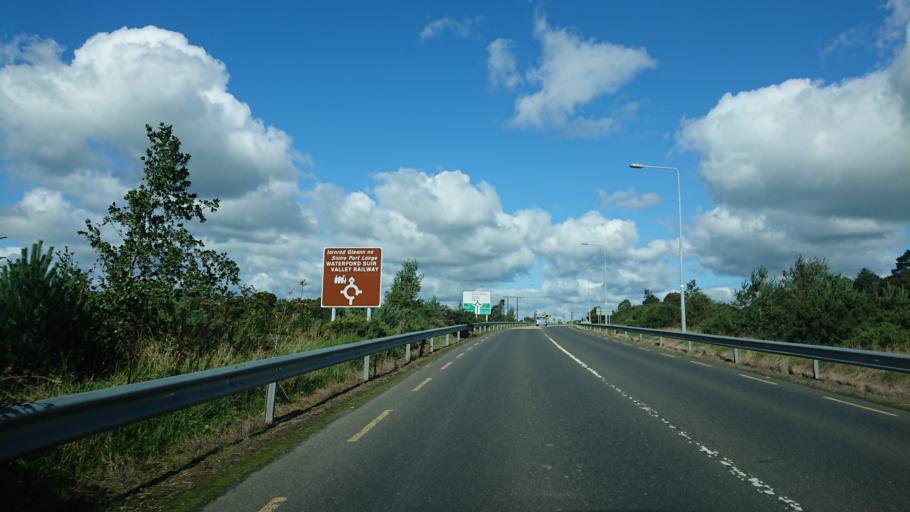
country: IE
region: Leinster
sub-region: Kilkenny
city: Mooncoin
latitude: 52.2398
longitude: -7.2474
